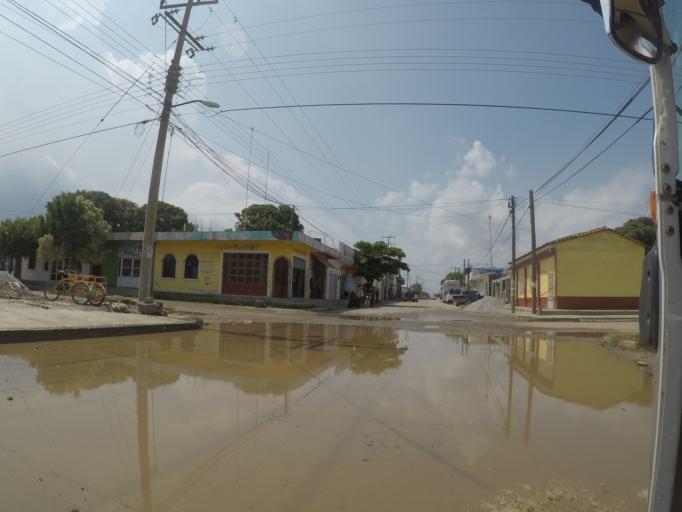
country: MX
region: Oaxaca
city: Union Hidalgo
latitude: 16.4716
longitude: -94.8300
